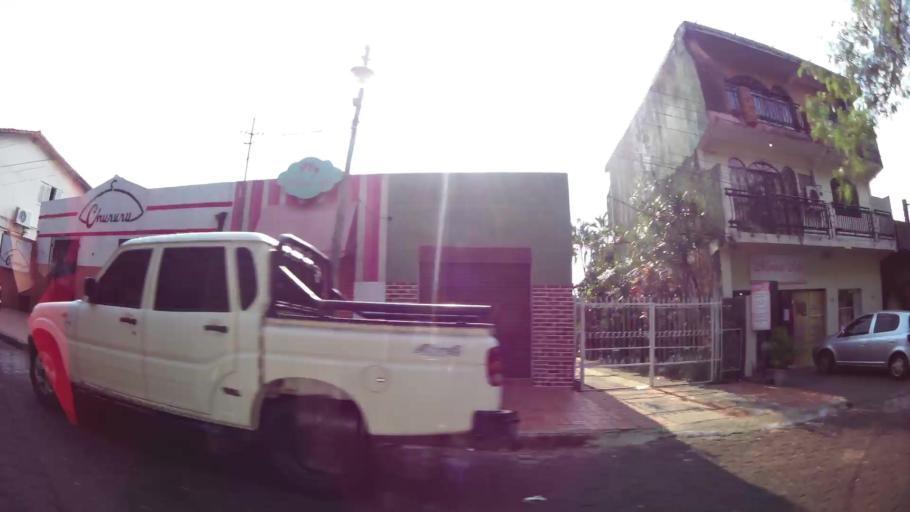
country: PY
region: Alto Parana
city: Presidente Franco
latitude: -25.5310
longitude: -54.6270
